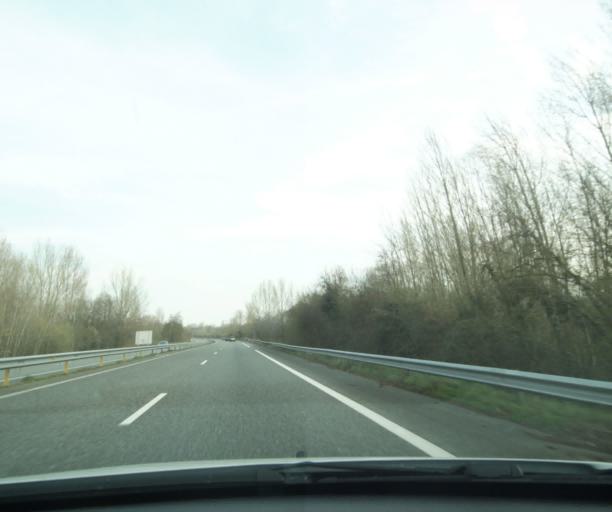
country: FR
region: Midi-Pyrenees
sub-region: Departement des Hautes-Pyrenees
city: Juillan
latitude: 43.2124
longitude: 0.0348
